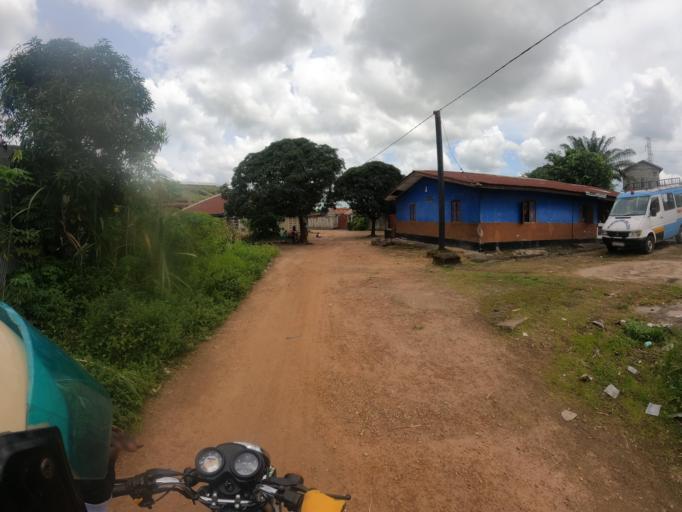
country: SL
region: Northern Province
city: Makeni
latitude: 8.8957
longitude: -12.0481
